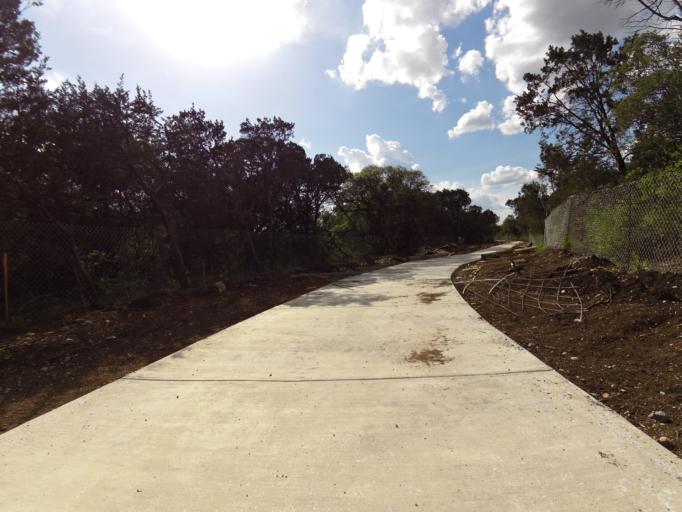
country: US
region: Texas
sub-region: Bexar County
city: Shavano Park
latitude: 29.5979
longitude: -98.5963
